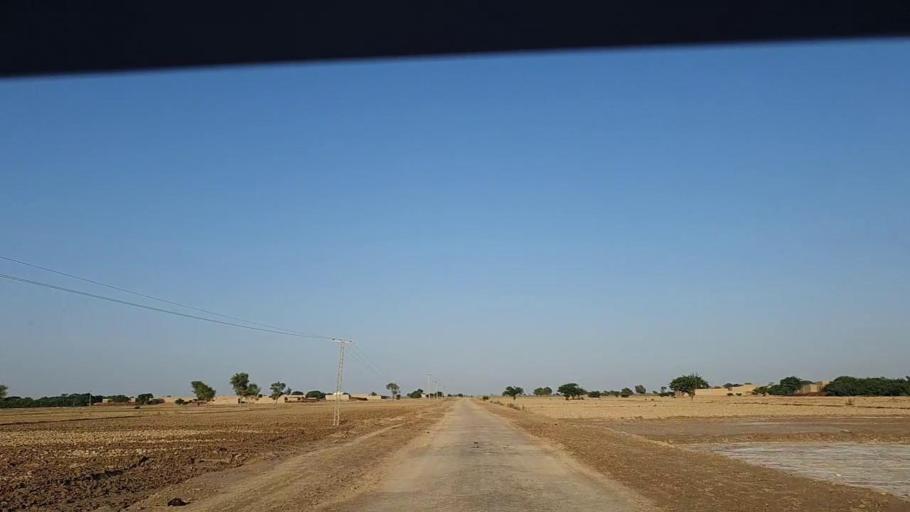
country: PK
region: Sindh
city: Johi
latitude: 26.7443
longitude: 67.6046
